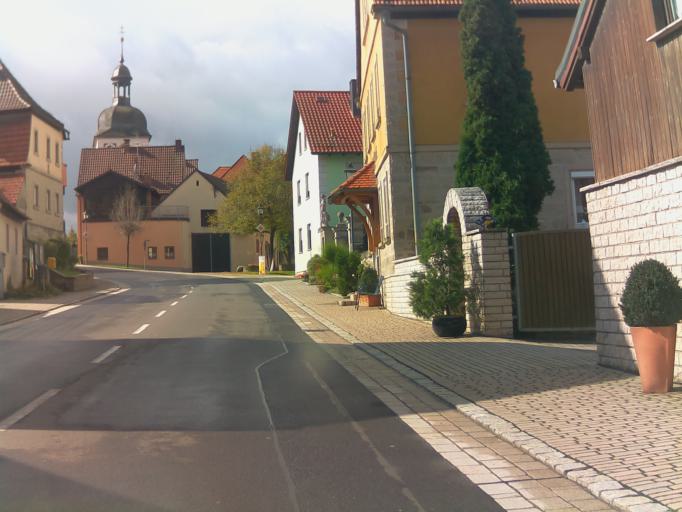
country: DE
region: Bavaria
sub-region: Upper Franconia
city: Burgwindheim
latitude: 49.8878
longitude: 10.5276
